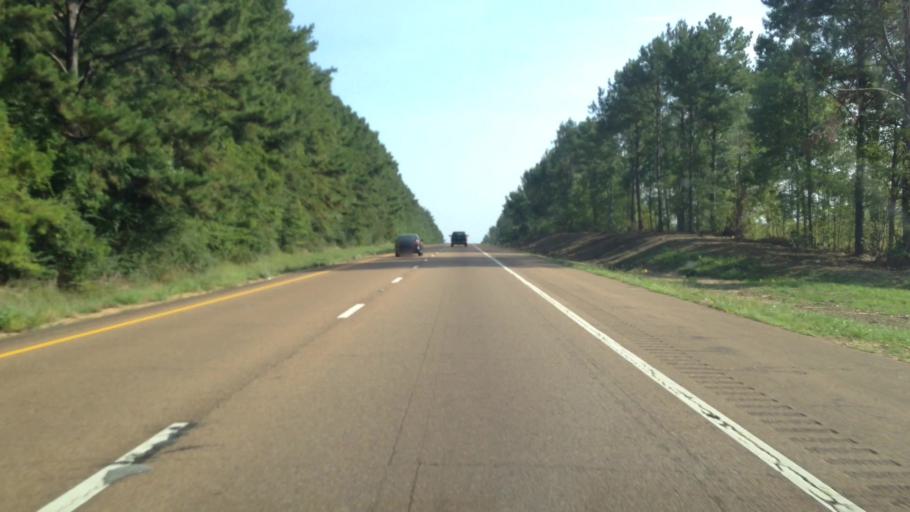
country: US
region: Mississippi
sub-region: Lincoln County
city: Brookhaven
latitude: 31.4630
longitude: -90.4788
